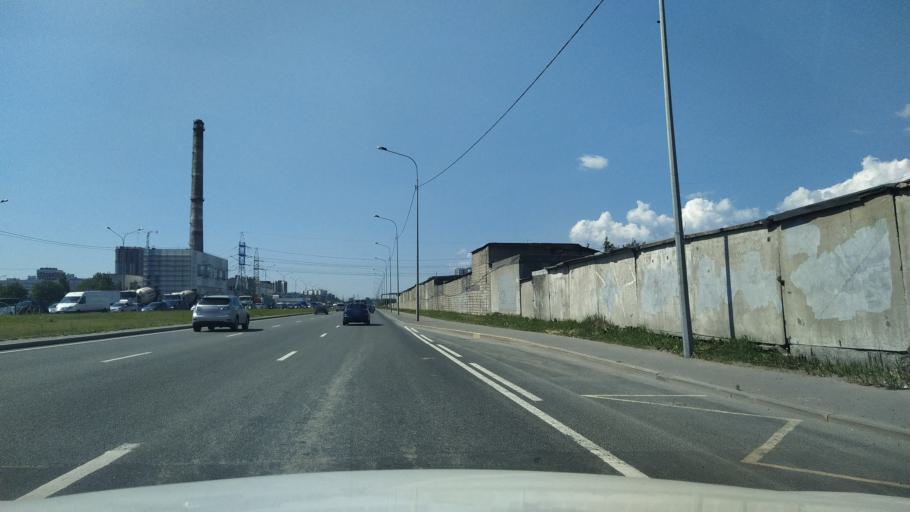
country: RU
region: Leningrad
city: Parnas
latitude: 60.0613
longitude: 30.3392
